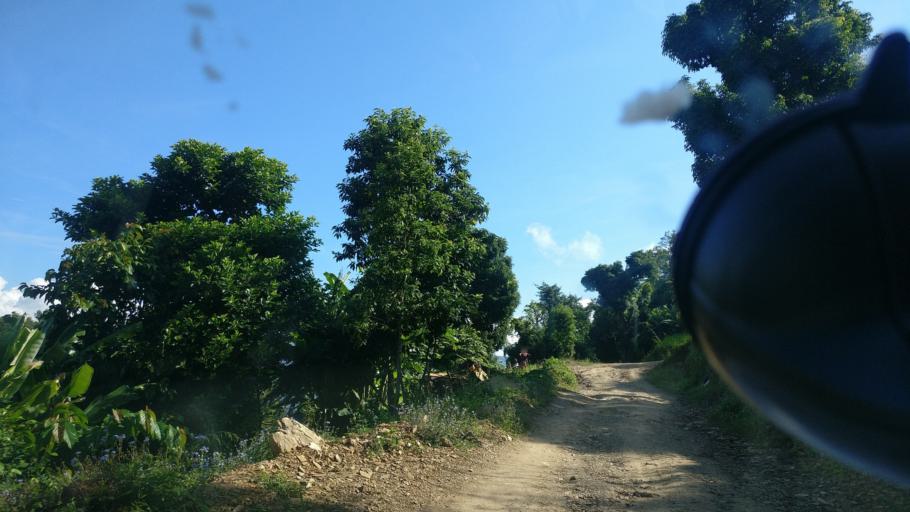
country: NP
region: Western Region
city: Baglung
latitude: 28.1425
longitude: 83.6462
